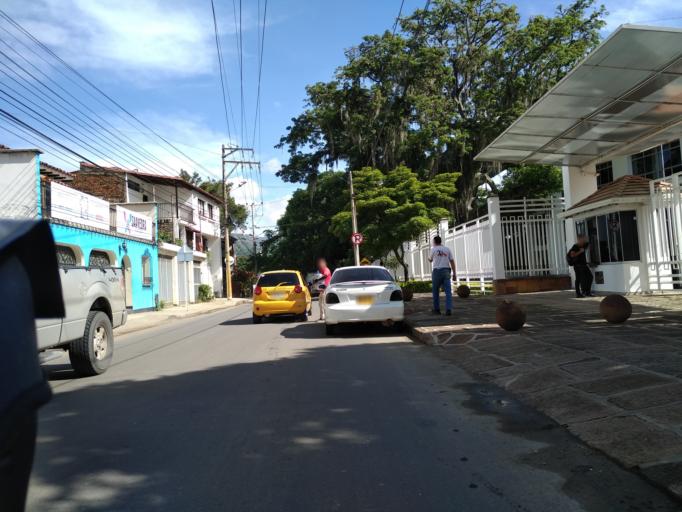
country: CO
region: Santander
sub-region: San Gil
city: San Gil
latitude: 6.5508
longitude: -73.1313
